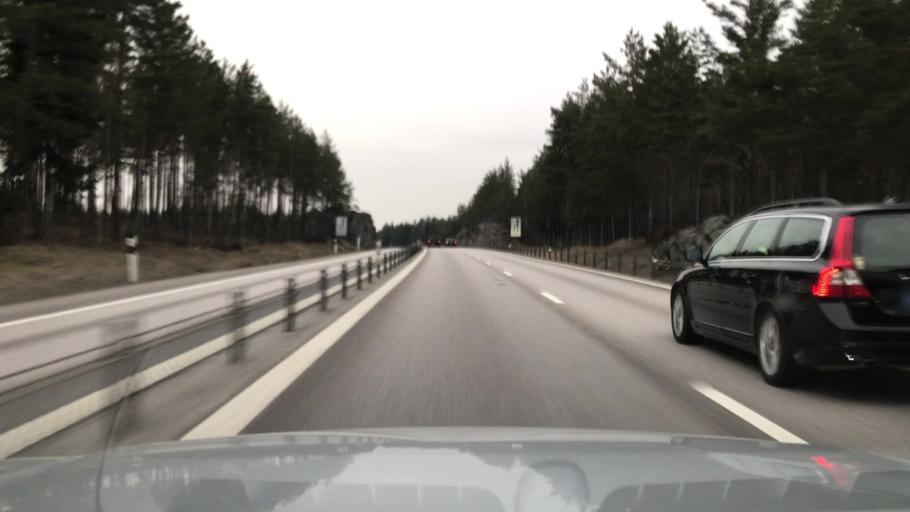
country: SE
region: OEstergoetland
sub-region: Valdemarsviks Kommun
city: Valdemarsvik
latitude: 58.2327
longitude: 16.5509
